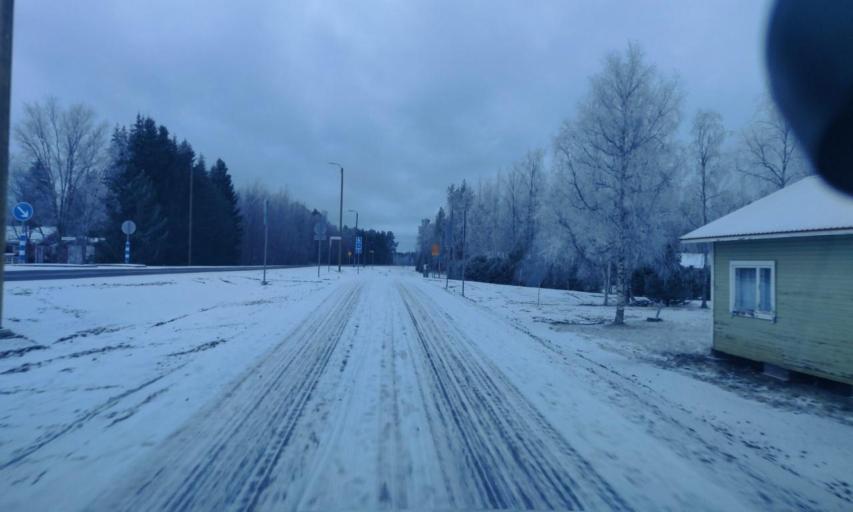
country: FI
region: Northern Ostrobothnia
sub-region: Oulu
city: Oulunsalo
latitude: 64.9854
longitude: 25.2644
